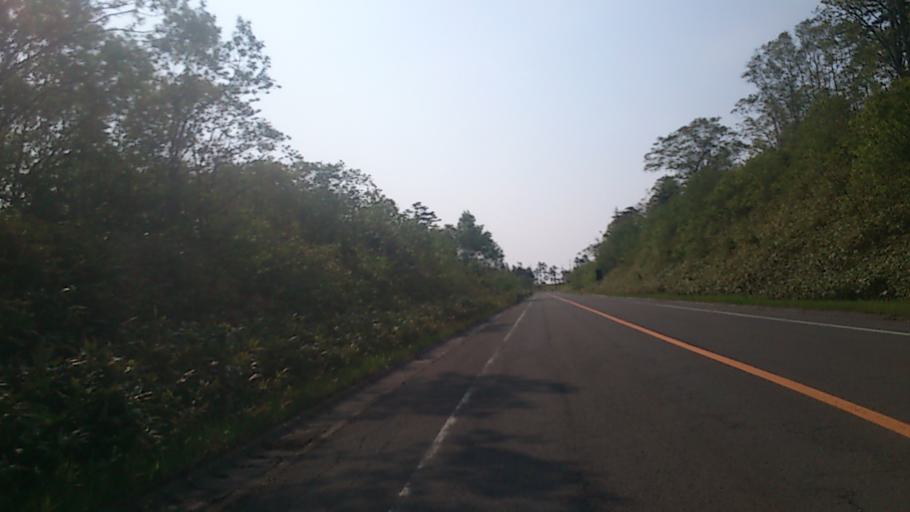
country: JP
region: Hokkaido
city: Bihoro
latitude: 43.4478
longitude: 144.2062
